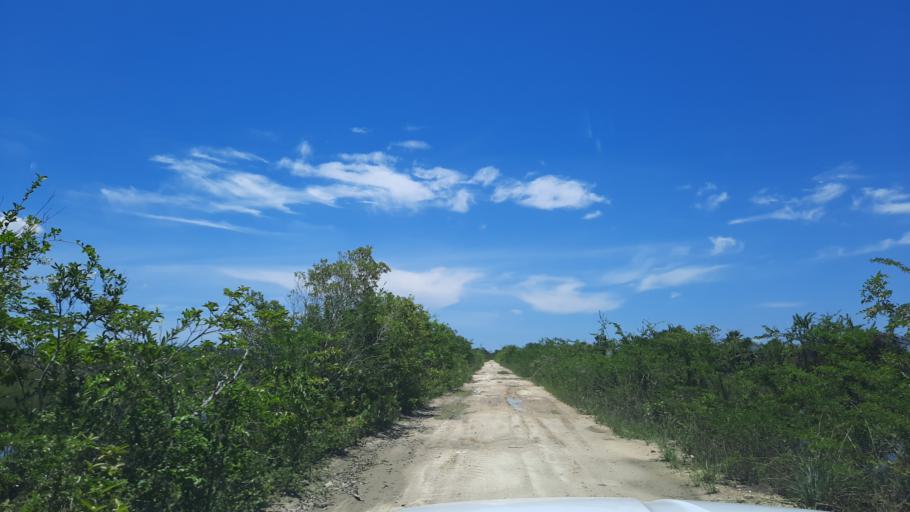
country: BZ
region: Cayo
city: Belmopan
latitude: 17.3824
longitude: -88.4929
